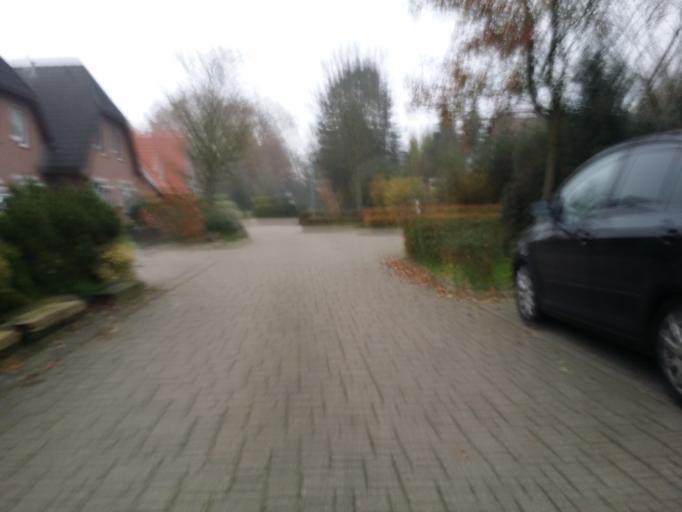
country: DE
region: Lower Saxony
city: Ganderkesee
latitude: 53.0240
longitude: 8.5612
